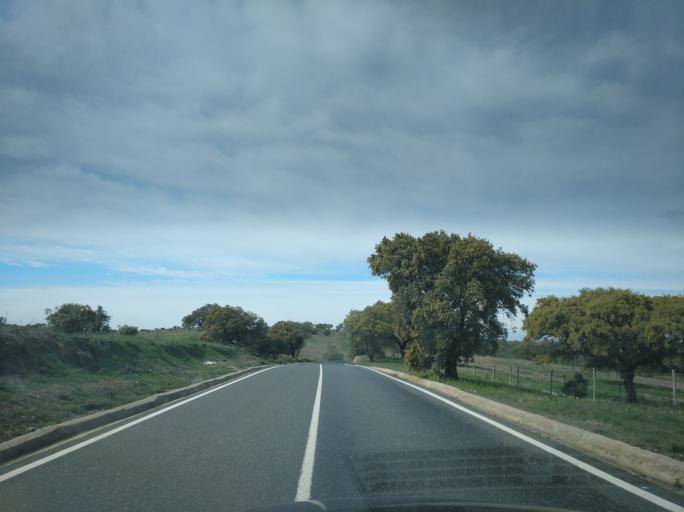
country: PT
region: Beja
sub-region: Mertola
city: Mertola
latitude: 37.7185
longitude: -7.7581
